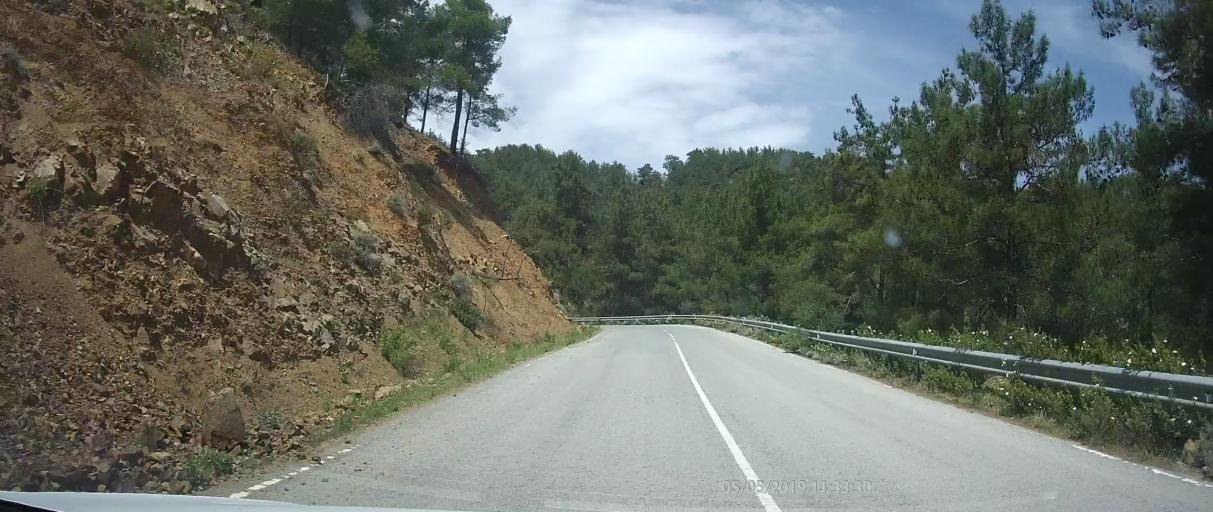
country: CY
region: Lefkosia
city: Kato Pyrgos
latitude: 34.9618
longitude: 32.6466
